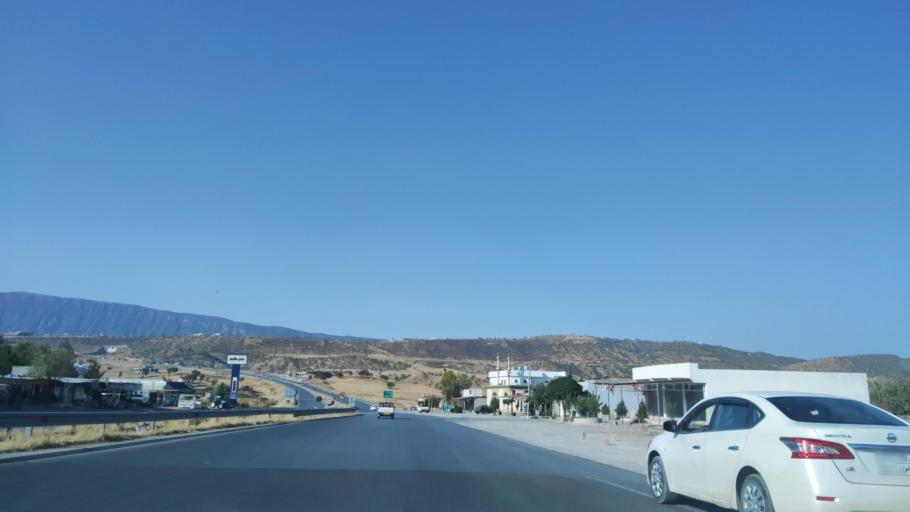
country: IQ
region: Arbil
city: Shaqlawah
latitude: 36.4548
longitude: 44.3823
